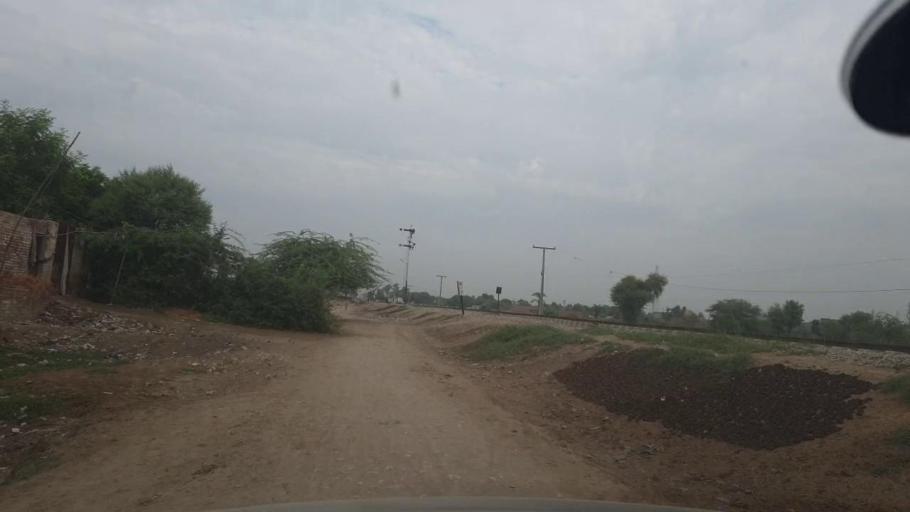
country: PK
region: Sindh
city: Jacobabad
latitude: 28.2668
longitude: 68.4430
